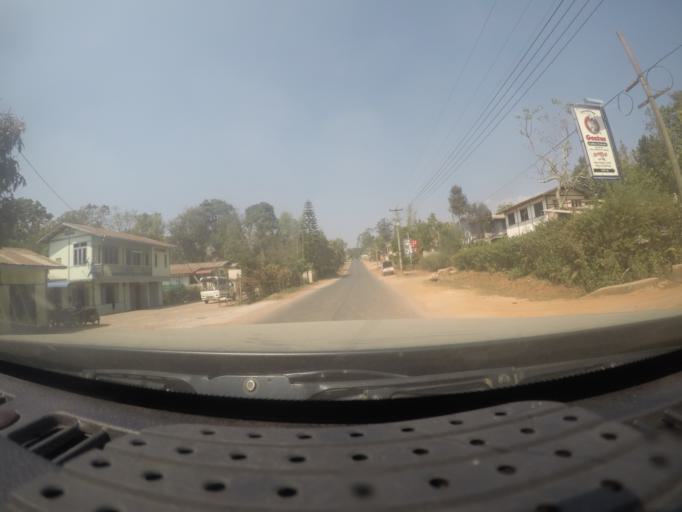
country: MM
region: Mandalay
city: Kyaukse
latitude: 21.1702
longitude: 96.4448
